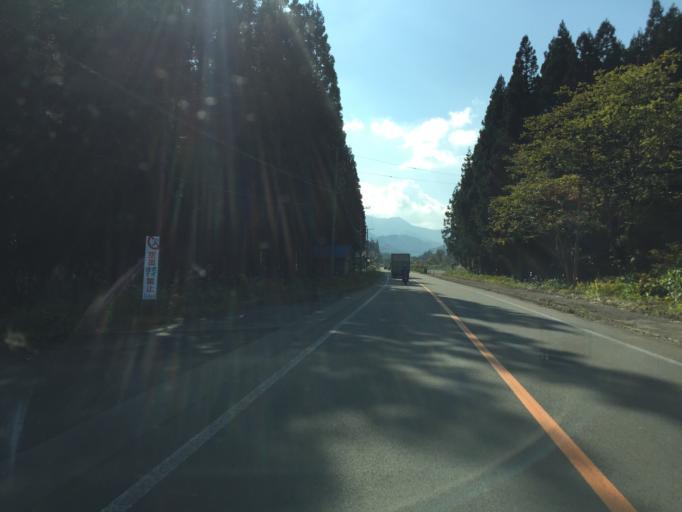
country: JP
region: Yamagata
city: Yonezawa
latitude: 37.8938
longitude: 140.0121
